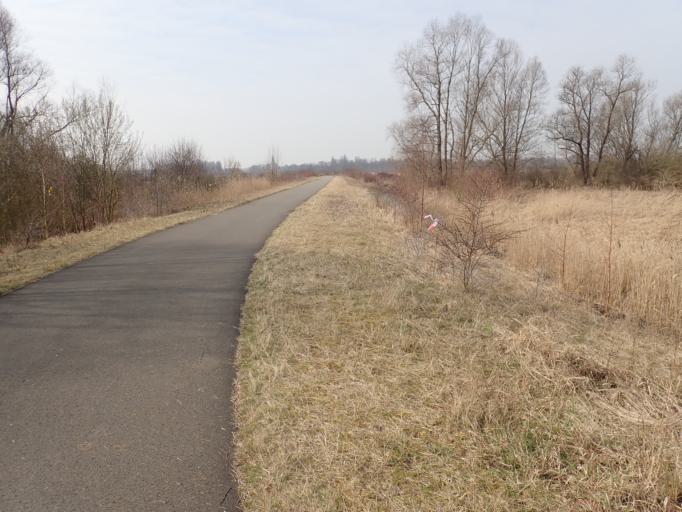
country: BE
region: Flanders
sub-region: Provincie Antwerpen
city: Hoboken
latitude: 51.2090
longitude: 4.3639
